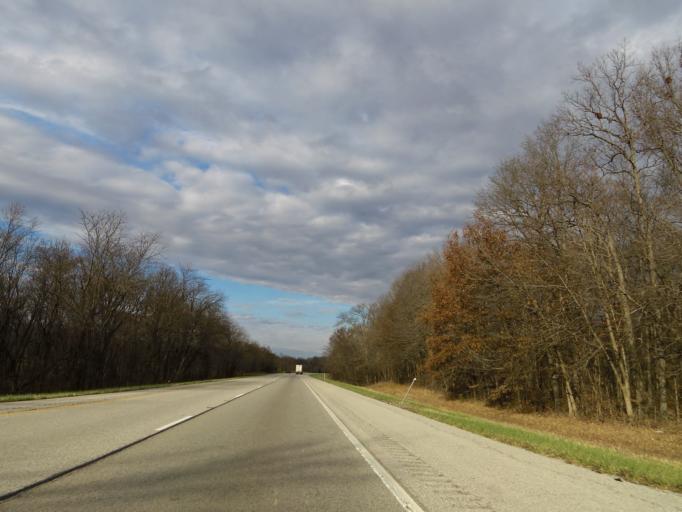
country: US
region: Illinois
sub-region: Washington County
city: Nashville
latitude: 38.4004
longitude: -89.3966
